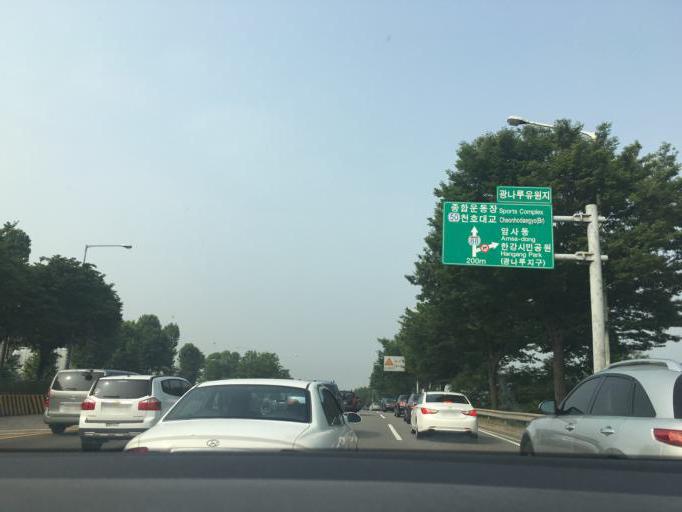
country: KR
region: Gyeonggi-do
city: Guri-si
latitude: 37.5621
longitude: 127.1292
